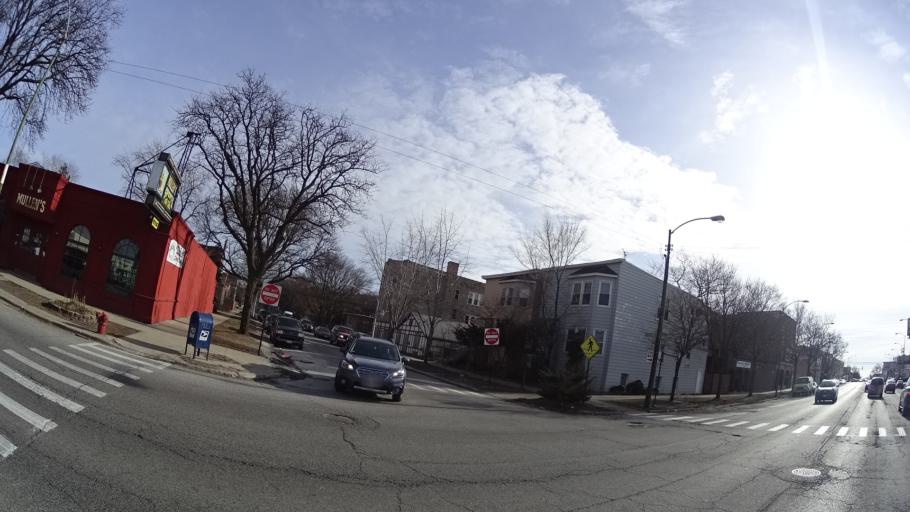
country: US
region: Illinois
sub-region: Cook County
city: Evanston
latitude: 42.0142
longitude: -87.6903
